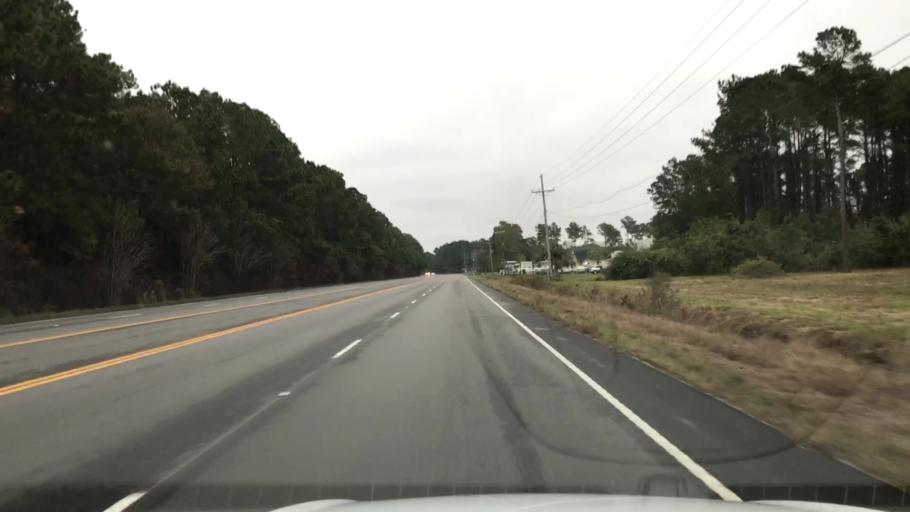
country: US
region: South Carolina
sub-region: Charleston County
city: Awendaw
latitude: 33.0966
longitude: -79.4740
